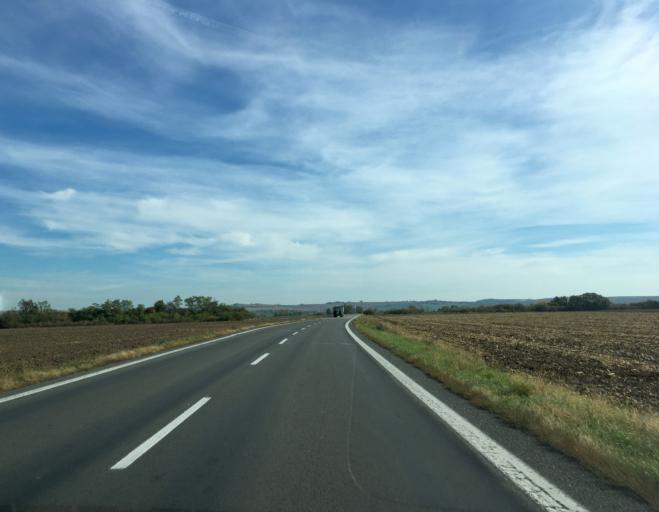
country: SK
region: Nitriansky
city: Zeliezovce
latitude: 48.1234
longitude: 18.6628
